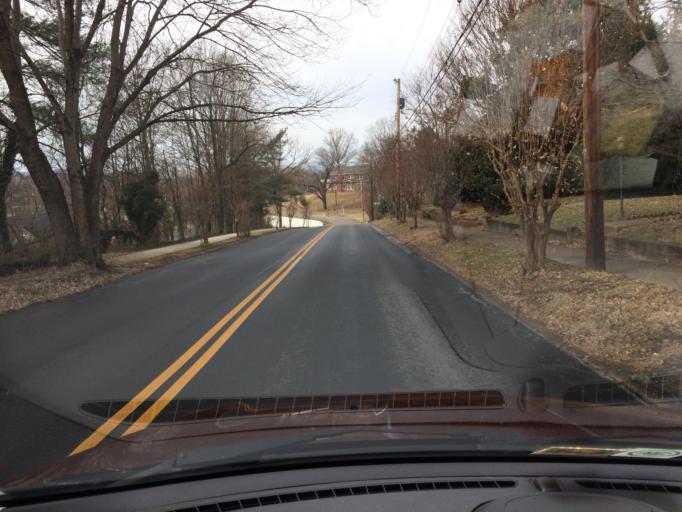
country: US
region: Virginia
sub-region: City of Bedford
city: Bedford
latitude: 37.3375
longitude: -79.5264
